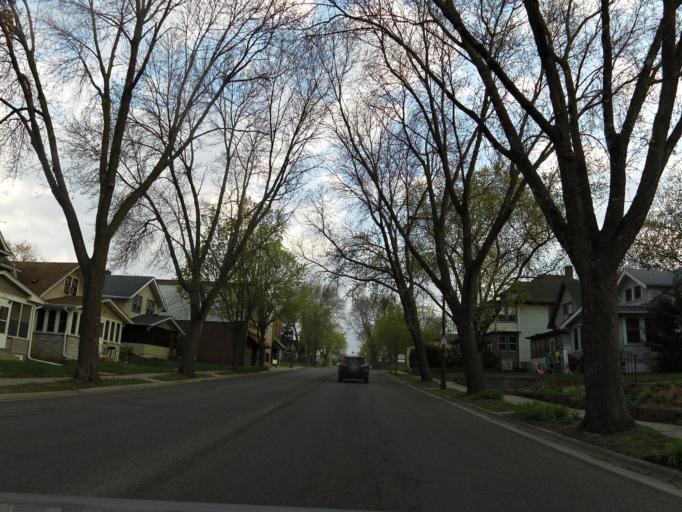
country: US
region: Minnesota
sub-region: Dakota County
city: West Saint Paul
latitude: 44.9214
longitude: -93.1019
